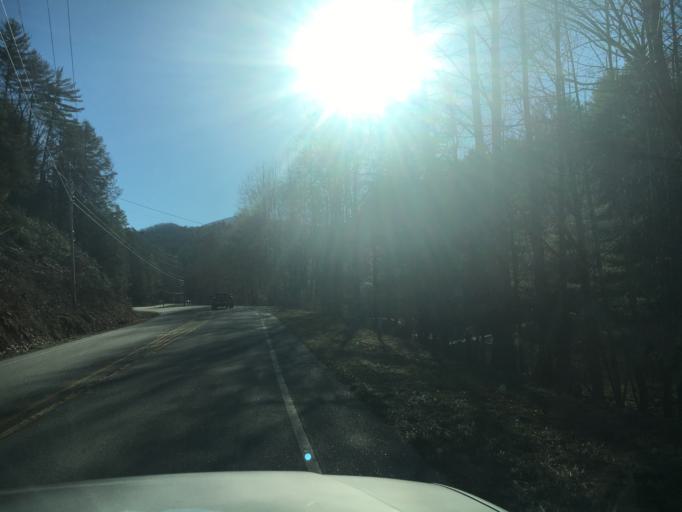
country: US
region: Georgia
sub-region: Union County
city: Blairsville
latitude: 34.7769
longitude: -83.9091
